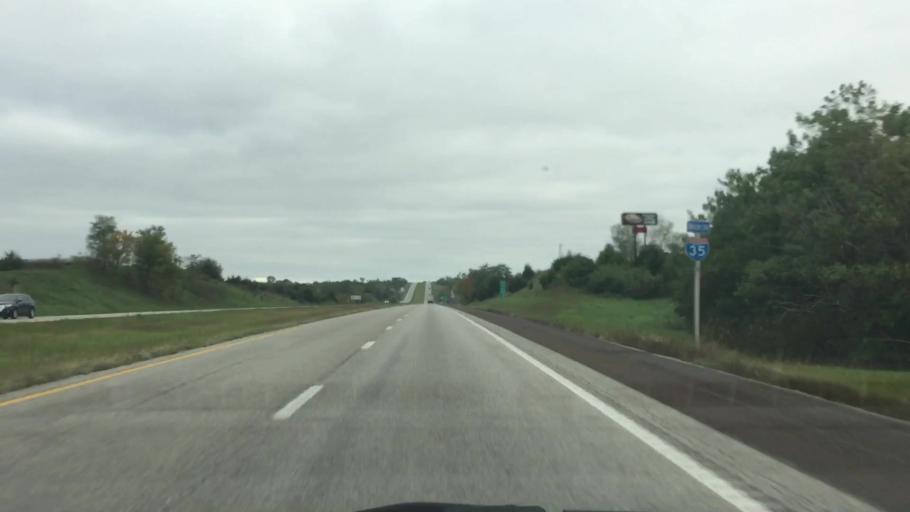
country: US
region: Missouri
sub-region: Daviess County
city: Gallatin
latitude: 39.9051
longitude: -94.1484
